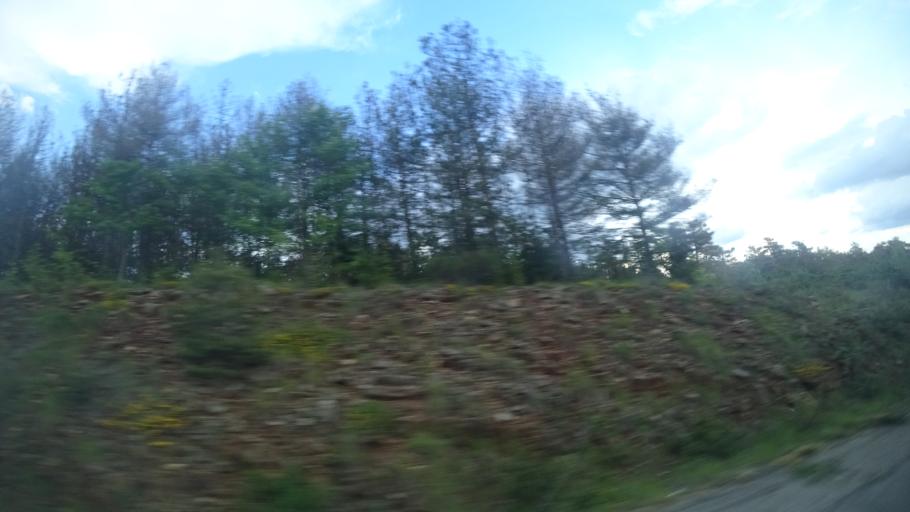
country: FR
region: Midi-Pyrenees
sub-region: Departement de l'Aveyron
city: Millau
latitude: 44.1926
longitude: 3.0237
